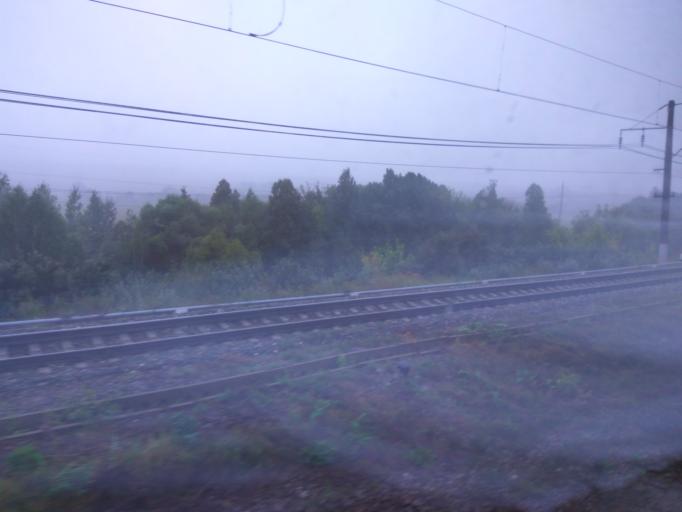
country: RU
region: Moskovskaya
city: Uzunovo
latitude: 54.5592
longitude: 38.6207
